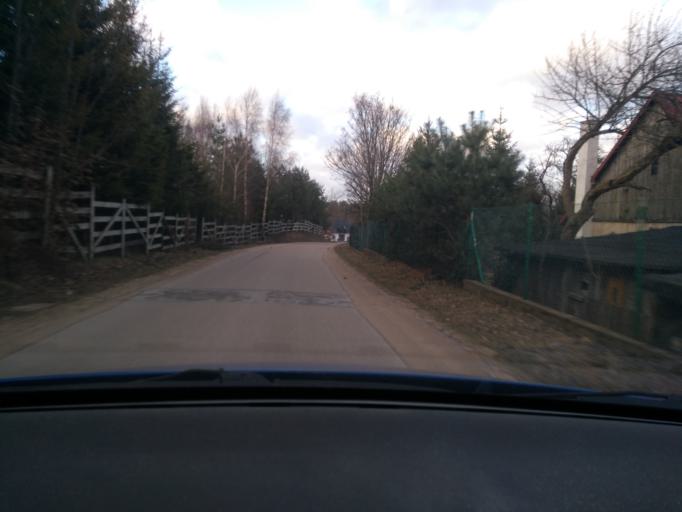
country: PL
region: Pomeranian Voivodeship
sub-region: Powiat kartuski
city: Przodkowo
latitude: 54.4110
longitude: 18.2330
